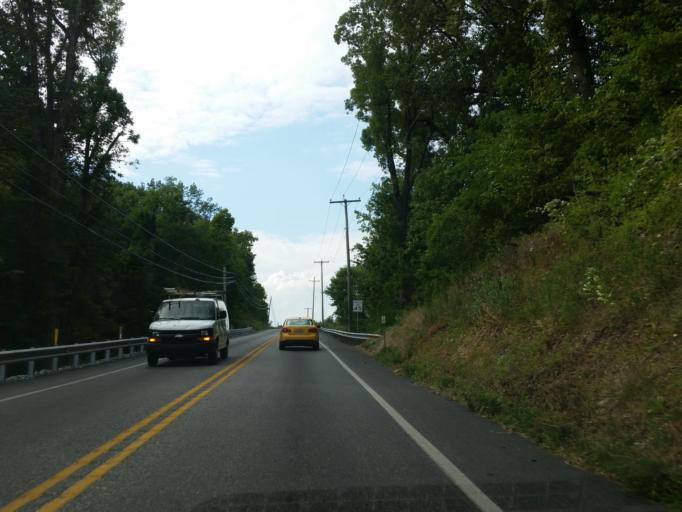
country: US
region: Pennsylvania
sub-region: Lebanon County
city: Annville
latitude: 40.3391
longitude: -76.5203
